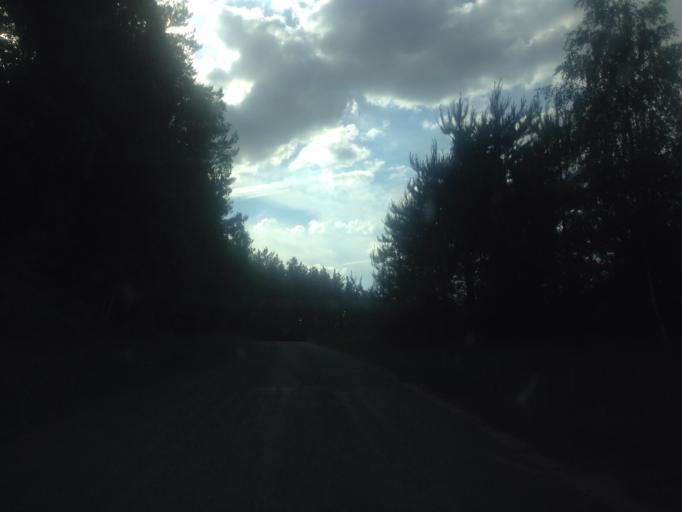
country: PL
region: Kujawsko-Pomorskie
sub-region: Powiat brodnicki
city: Brzozie
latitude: 53.3114
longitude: 19.5583
